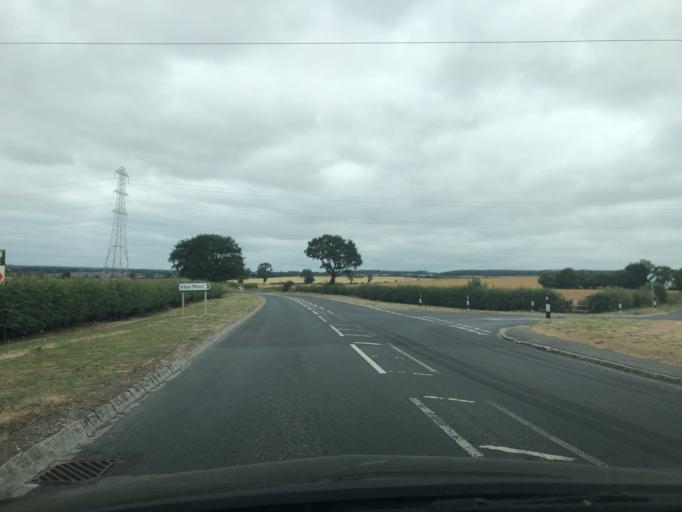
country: GB
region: England
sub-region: North Yorkshire
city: East Ayton
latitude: 54.2454
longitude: -0.4510
